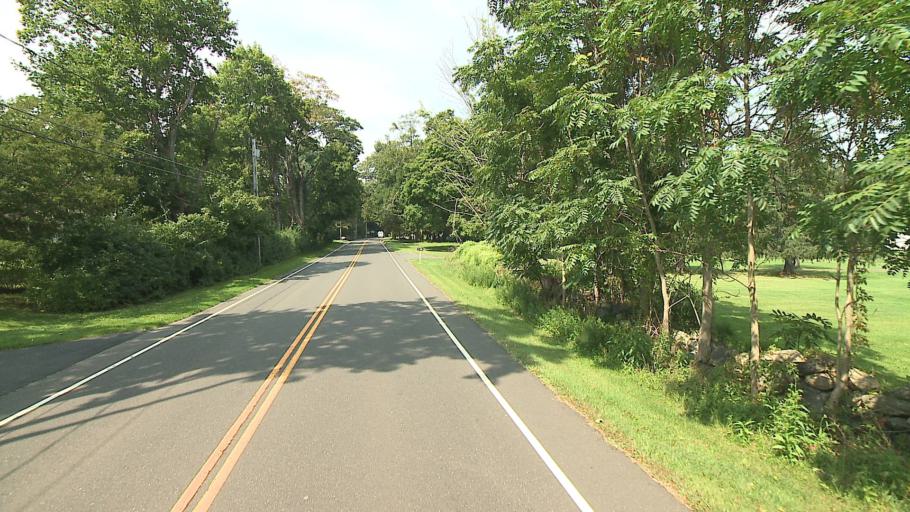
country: US
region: New York
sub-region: Putnam County
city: Peach Lake
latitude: 41.3274
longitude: -73.5440
